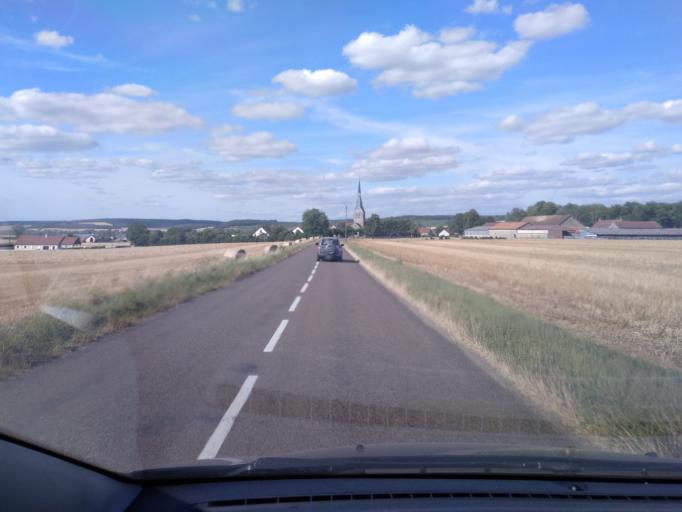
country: FR
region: Bourgogne
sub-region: Departement de la Cote-d'Or
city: Chatillon-sur-Seine
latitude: 47.9399
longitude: 4.6487
